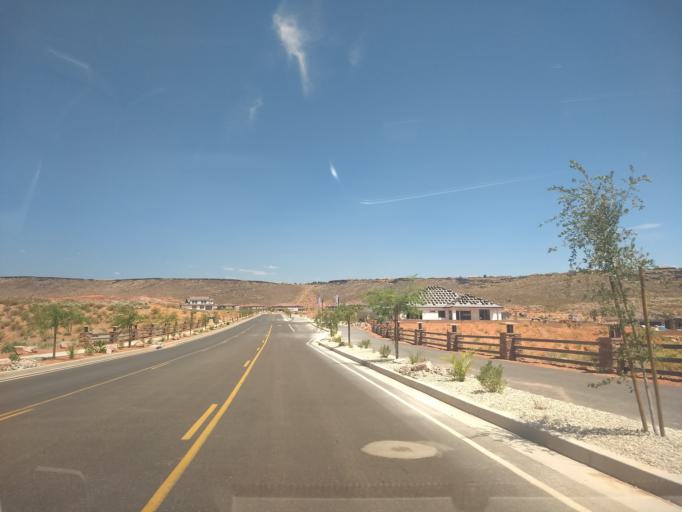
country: US
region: Utah
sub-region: Washington County
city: Washington
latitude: 37.1440
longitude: -113.4775
